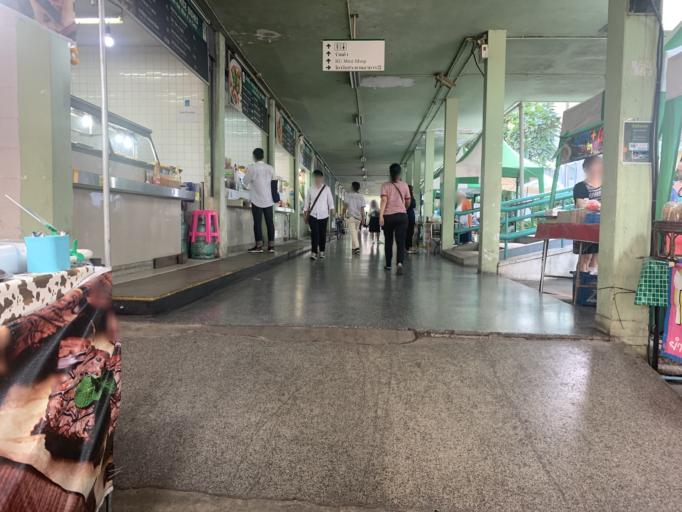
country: TH
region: Bangkok
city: Chatuchak
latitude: 13.8487
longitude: 100.5671
